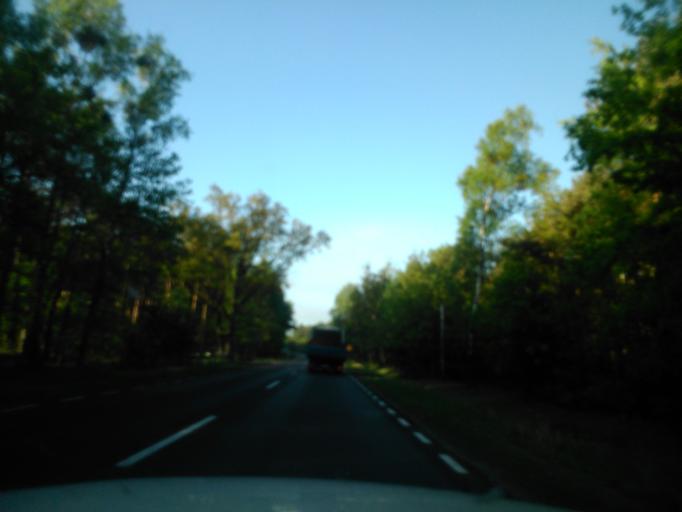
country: PL
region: Masovian Voivodeship
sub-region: Powiat sochaczewski
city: Mlodzieszyn
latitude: 52.3195
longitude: 20.2078
